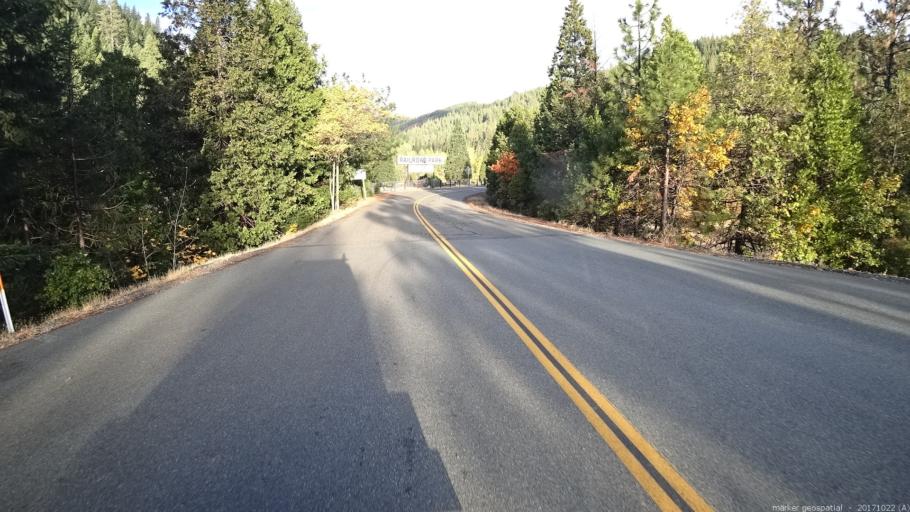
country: US
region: California
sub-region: Siskiyou County
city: Dunsmuir
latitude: 41.1831
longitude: -122.2913
